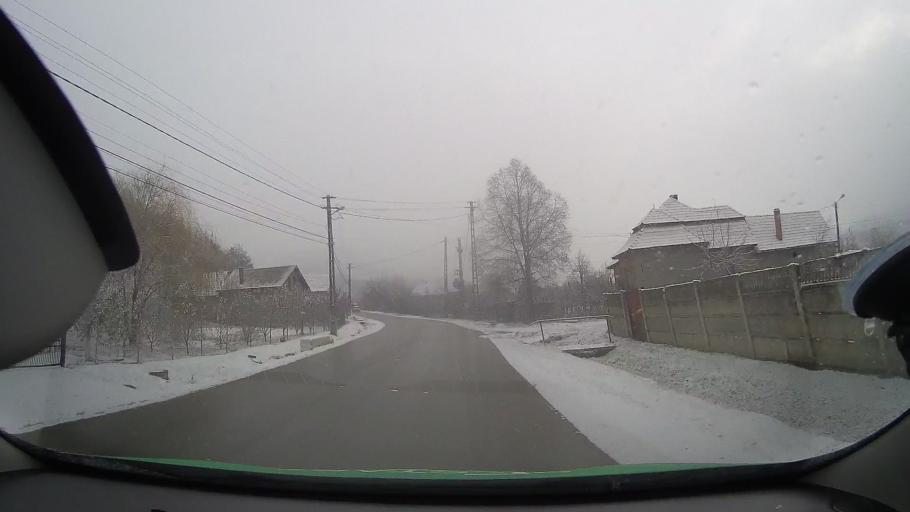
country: RO
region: Alba
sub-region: Municipiul Aiud
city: Ciumbrud
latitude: 46.3108
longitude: 23.7897
